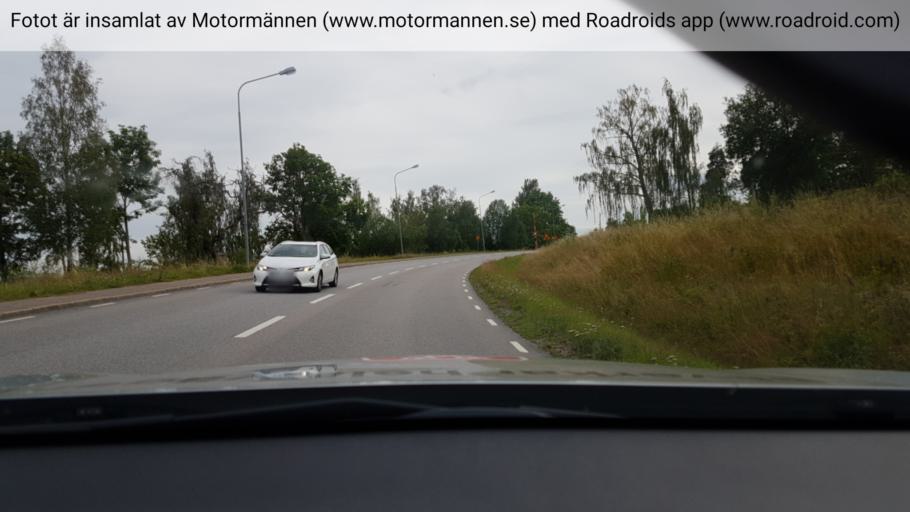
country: SE
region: Vaestra Goetaland
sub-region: Bengtsfors Kommun
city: Billingsfors
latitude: 58.9865
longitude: 12.2521
